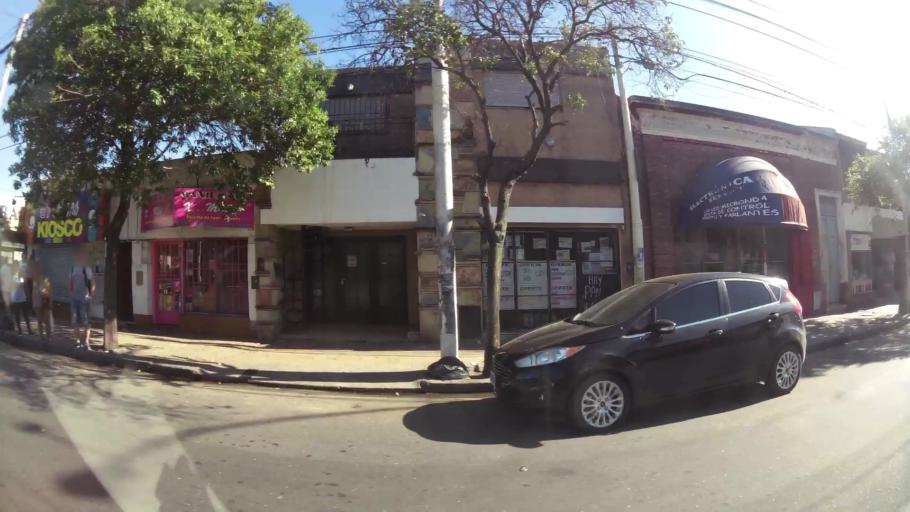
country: AR
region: Cordoba
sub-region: Departamento de Capital
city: Cordoba
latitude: -31.4236
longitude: -64.1460
